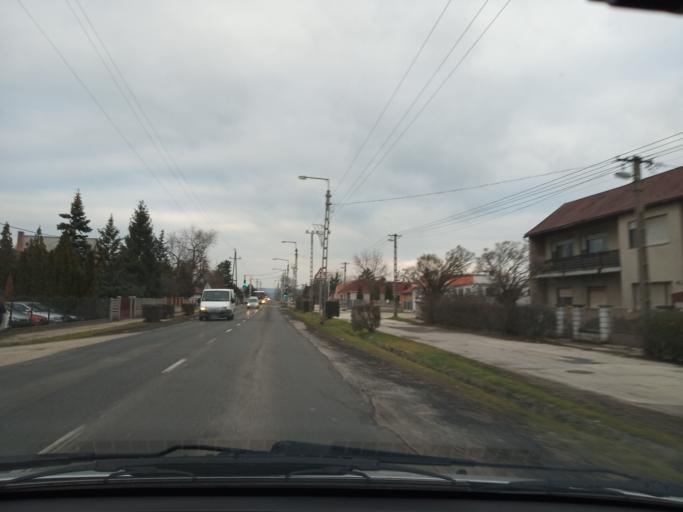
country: HU
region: Komarom-Esztergom
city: Dorog
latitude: 47.7411
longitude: 18.7274
